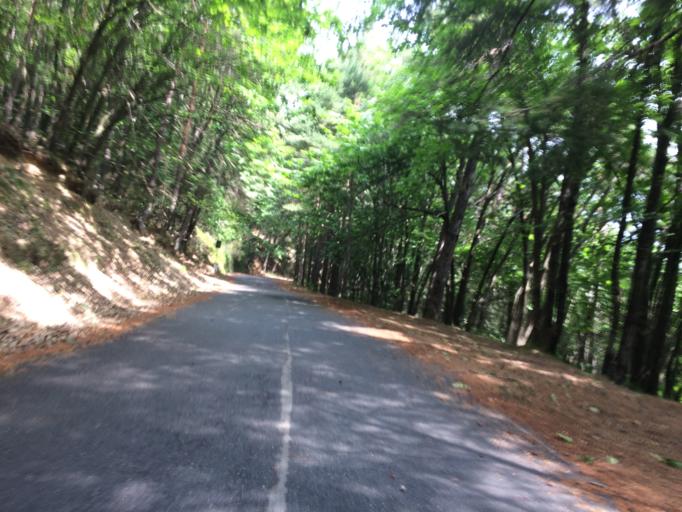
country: IT
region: Liguria
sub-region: Provincia di Imperia
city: Bajardo
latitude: 43.8808
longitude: 7.7404
